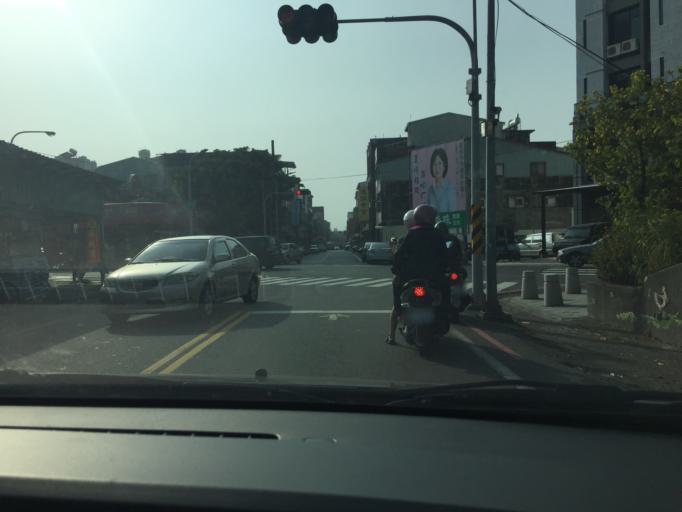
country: TW
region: Taiwan
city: Xinying
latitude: 23.1852
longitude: 120.2527
